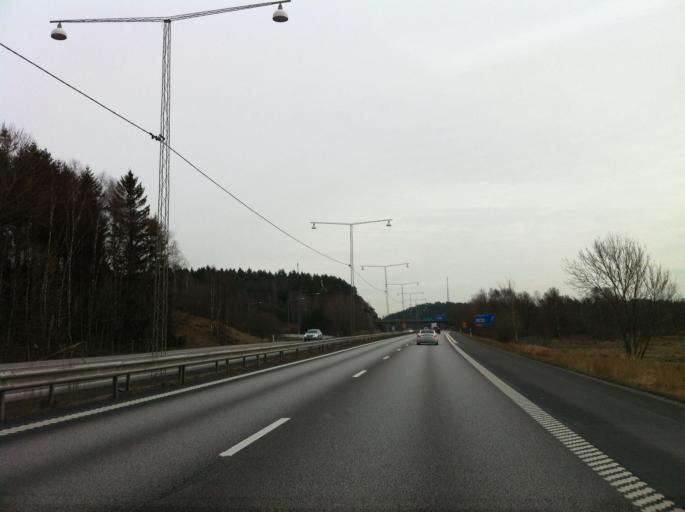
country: SE
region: Vaestra Goetaland
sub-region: Kungalvs Kommun
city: Kode
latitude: 57.9236
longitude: 11.8785
